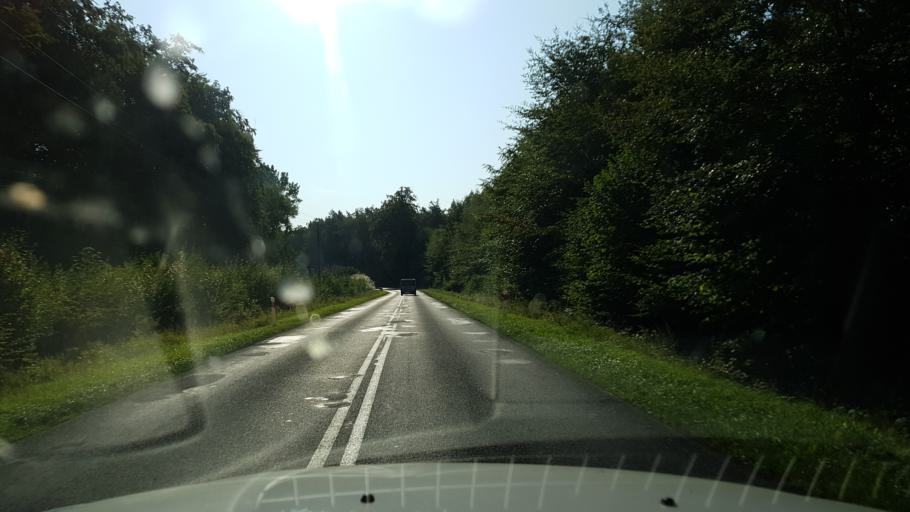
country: PL
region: West Pomeranian Voivodeship
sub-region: Powiat lobeski
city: Resko
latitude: 53.7802
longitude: 15.3410
